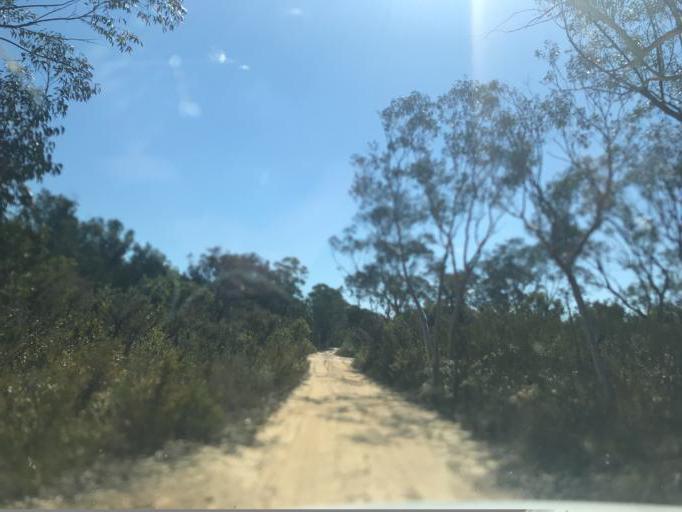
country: AU
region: New South Wales
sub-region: Wyong Shire
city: Little Jilliby
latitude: -33.1563
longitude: 151.0993
